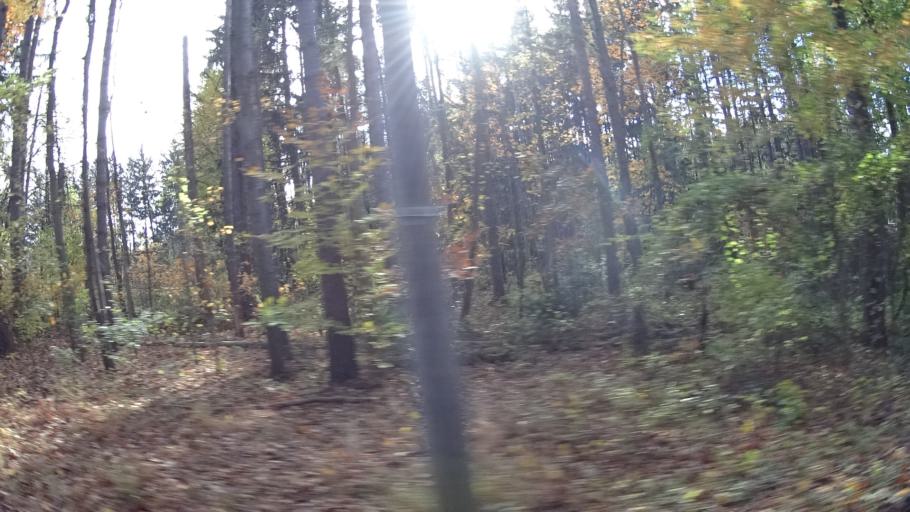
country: US
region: New Jersey
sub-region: Morris County
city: Morristown
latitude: 40.7527
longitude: -74.5159
